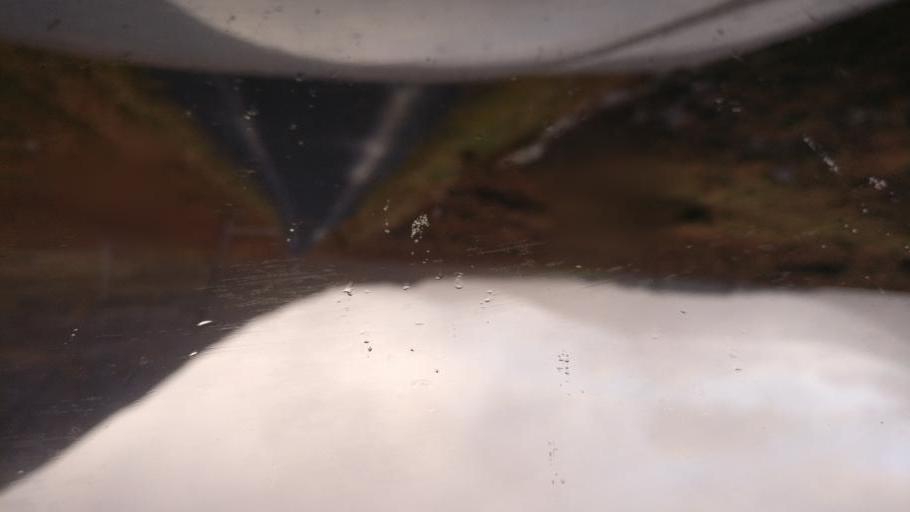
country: IE
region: Connaught
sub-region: County Galway
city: Clifden
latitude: 53.5172
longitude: -9.7190
